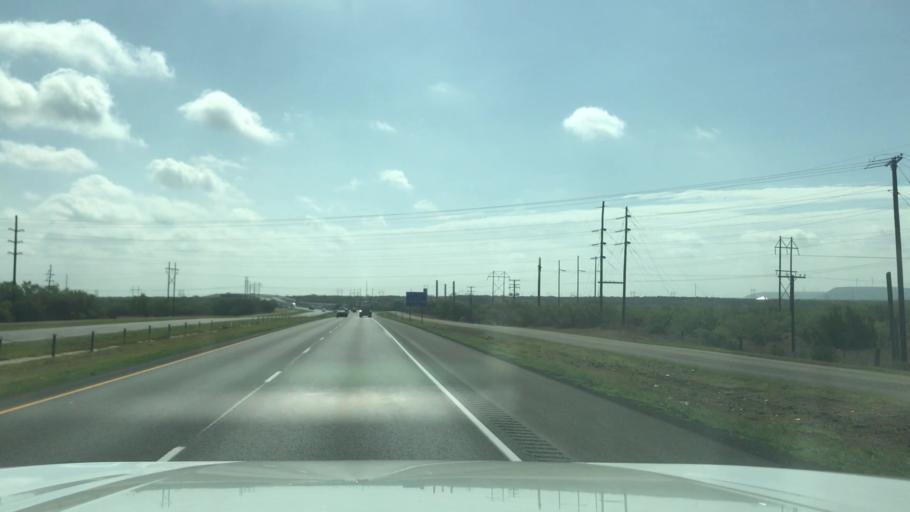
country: US
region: Texas
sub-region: Nolan County
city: Sweetwater
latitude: 32.4909
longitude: -100.2463
